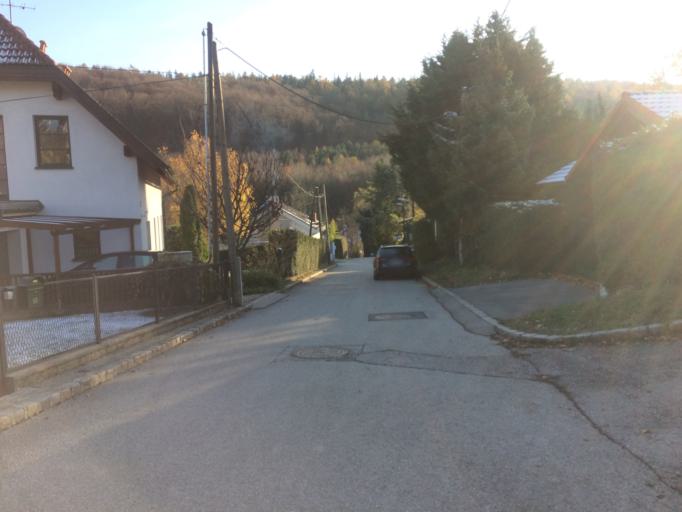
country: AT
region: Lower Austria
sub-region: Politischer Bezirk Wien-Umgebung
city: Gablitz
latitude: 48.2210
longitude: 16.1487
